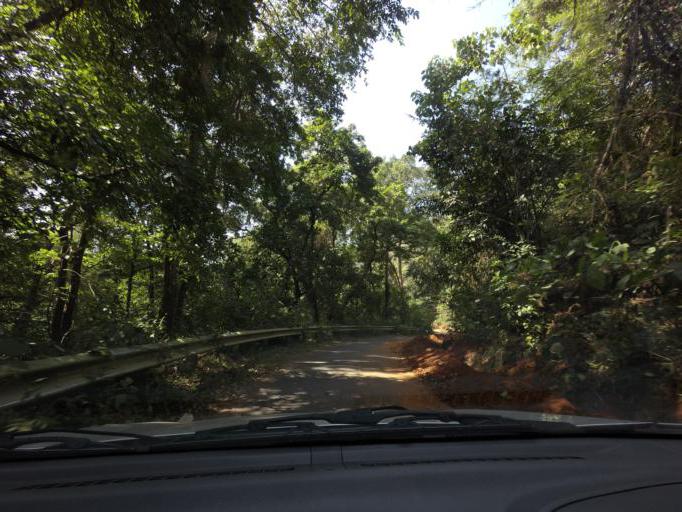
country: IN
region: Karnataka
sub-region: Kodagu
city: Somvarpet
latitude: 12.6916
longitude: 75.6259
